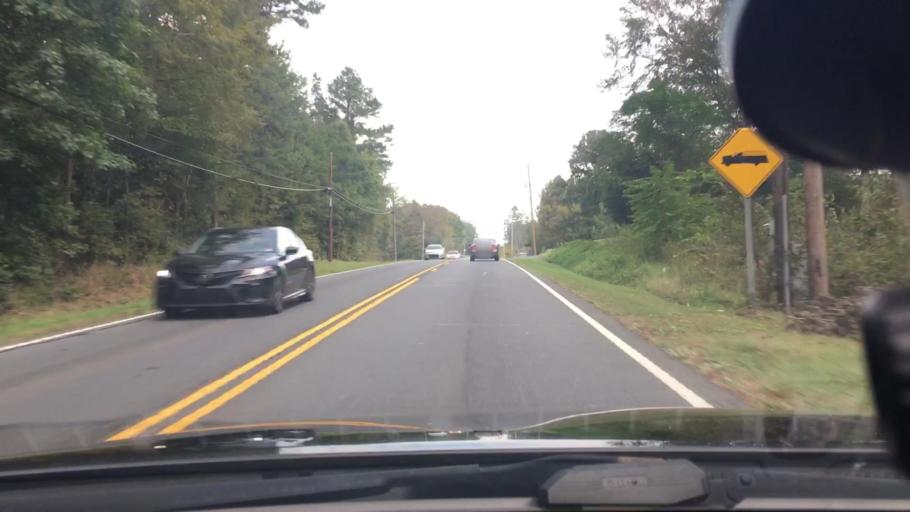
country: US
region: North Carolina
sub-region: Stanly County
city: Albemarle
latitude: 35.3258
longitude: -80.1303
